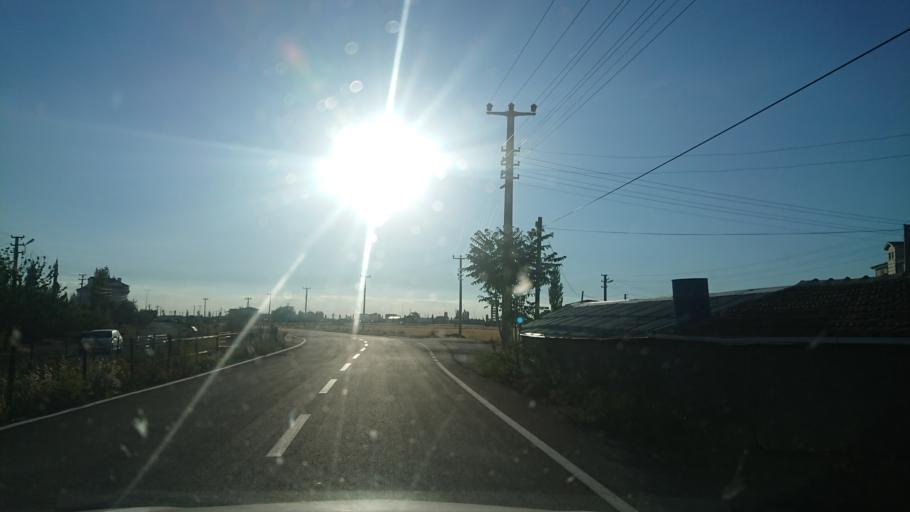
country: TR
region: Aksaray
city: Aksaray
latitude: 38.3913
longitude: 33.9927
